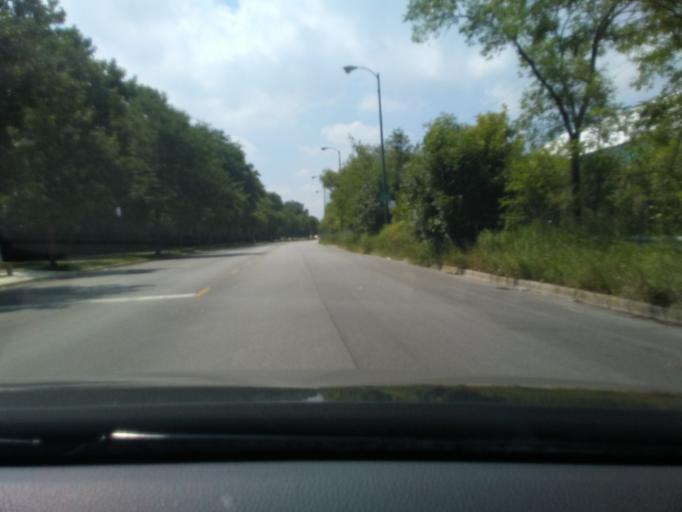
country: US
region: Illinois
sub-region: Cook County
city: Lincolnwood
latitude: 42.0155
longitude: -87.7088
